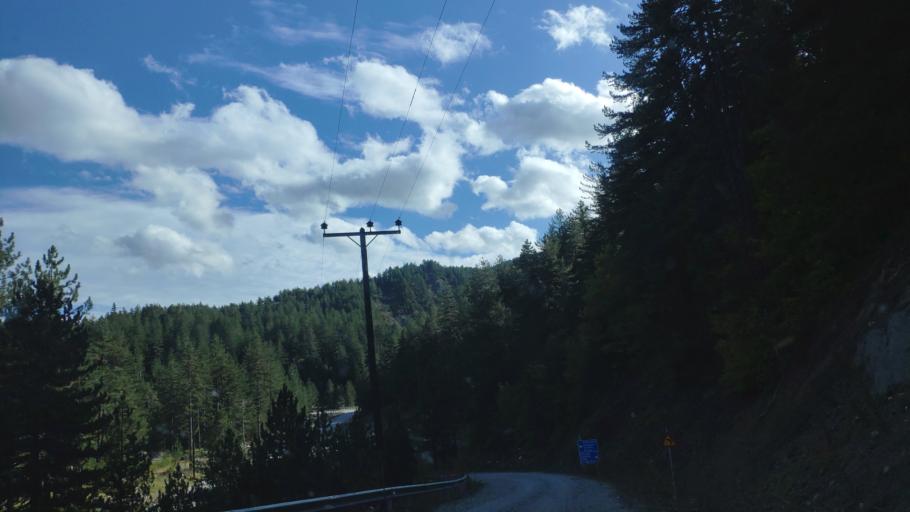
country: AL
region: Korce
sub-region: Rrethi i Devollit
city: Miras
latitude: 40.4122
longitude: 20.8733
